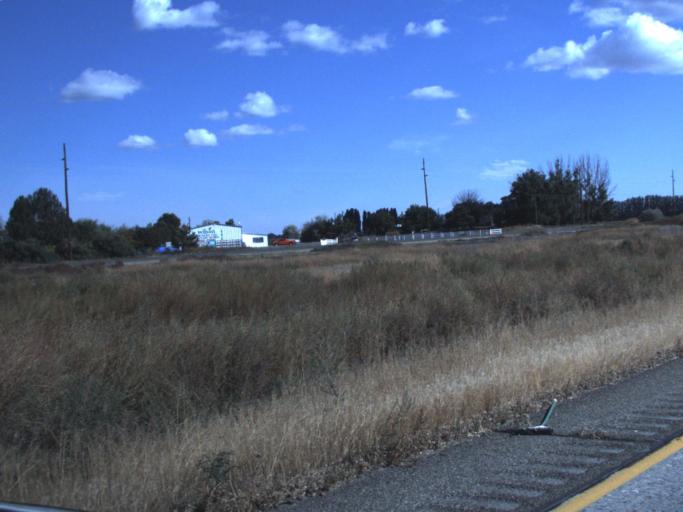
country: US
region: Washington
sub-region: Yakima County
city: Grandview
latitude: 46.2823
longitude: -119.9403
